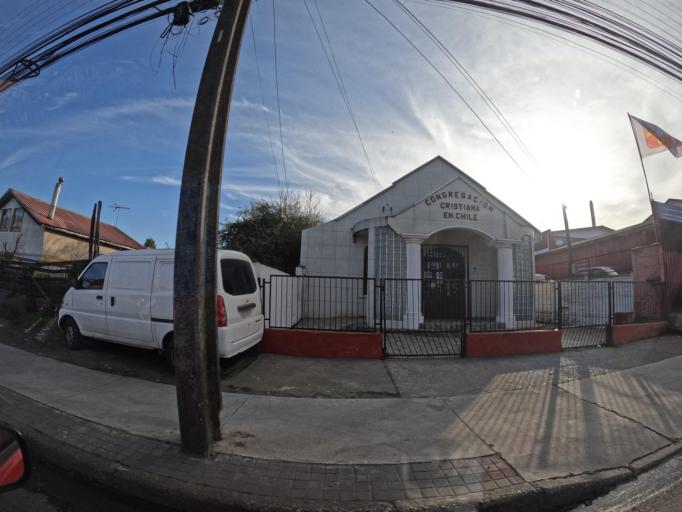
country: CL
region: Biobio
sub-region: Provincia de Concepcion
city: Concepcion
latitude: -36.7931
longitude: -73.0456
